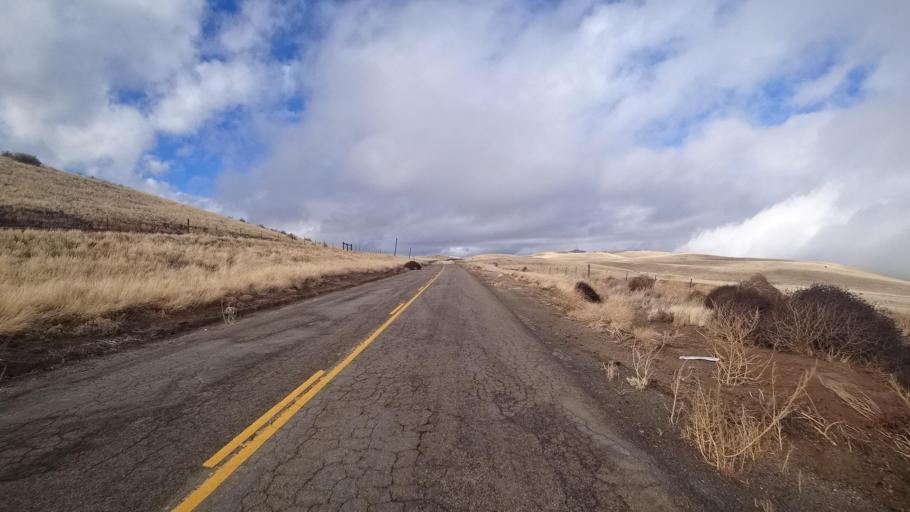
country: US
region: California
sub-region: Kern County
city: Maricopa
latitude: 34.9052
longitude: -119.3805
